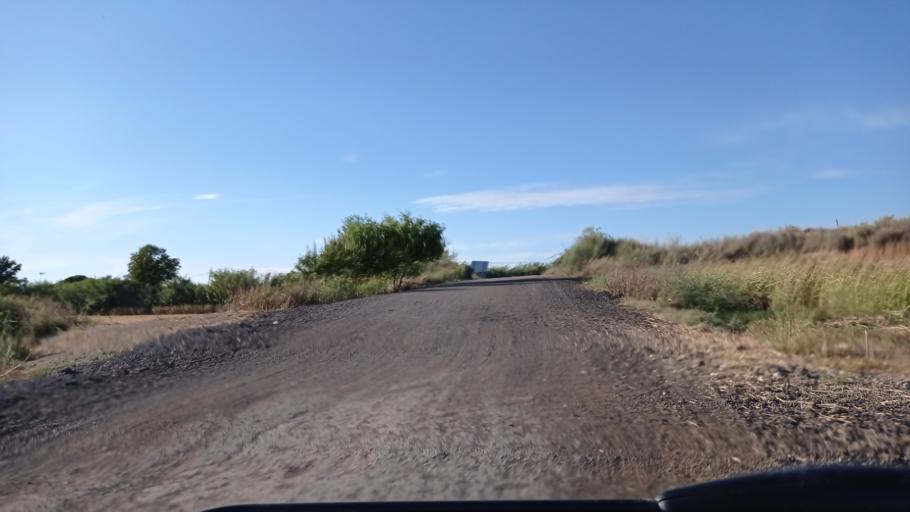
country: ES
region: Aragon
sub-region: Provincia de Zaragoza
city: Oliver-Valdefierro, Oliver, Valdefierro
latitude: 41.6623
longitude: -0.9499
